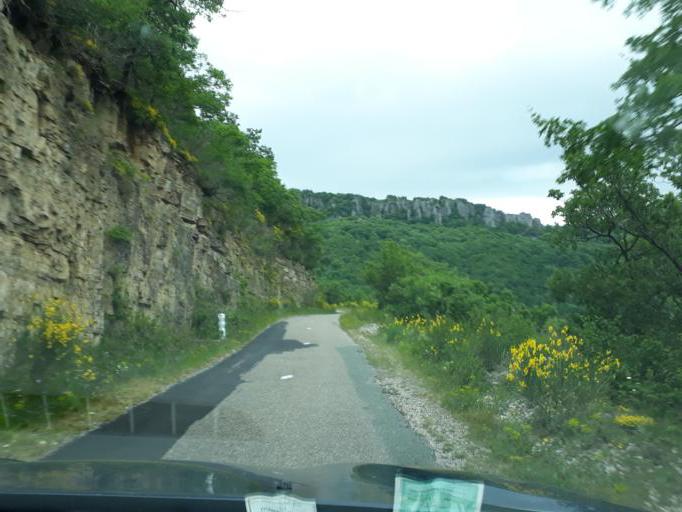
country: FR
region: Languedoc-Roussillon
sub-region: Departement de l'Herault
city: Lodeve
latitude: 43.7939
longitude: 3.2728
